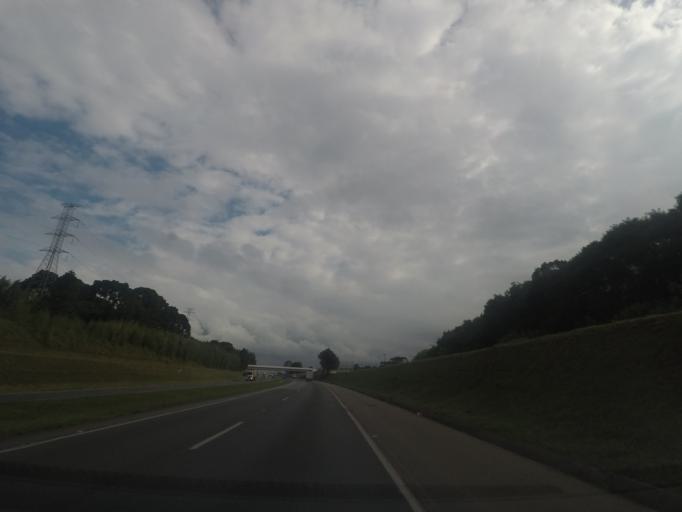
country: BR
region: Parana
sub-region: Piraquara
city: Piraquara
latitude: -25.4834
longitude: -49.1072
